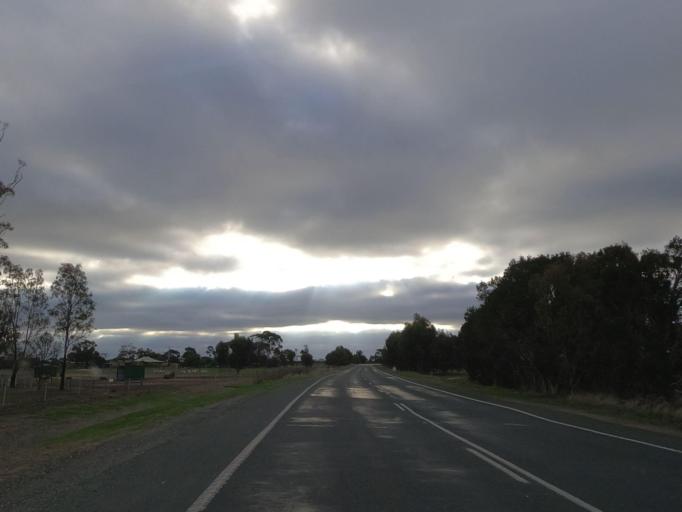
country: AU
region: Victoria
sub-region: Swan Hill
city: Swan Hill
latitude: -35.7320
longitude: 143.8961
